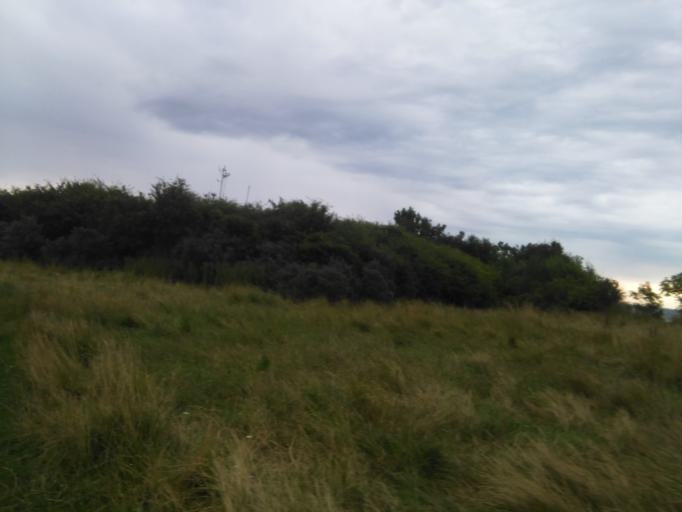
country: DK
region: Central Jutland
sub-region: Arhus Kommune
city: Hjortshoj
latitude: 56.2073
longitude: 10.2848
